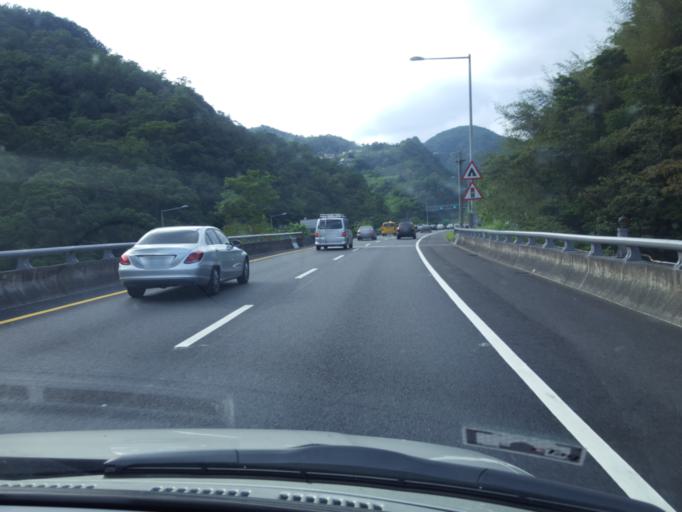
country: TW
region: Taiwan
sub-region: Keelung
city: Keelung
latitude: 24.9469
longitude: 121.7067
